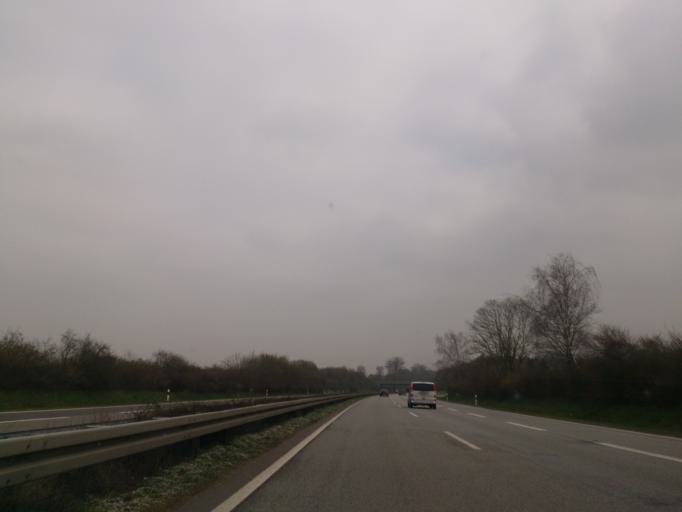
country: DE
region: North Rhine-Westphalia
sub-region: Regierungsbezirk Dusseldorf
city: Schwalmtal
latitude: 51.2069
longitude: 6.2537
